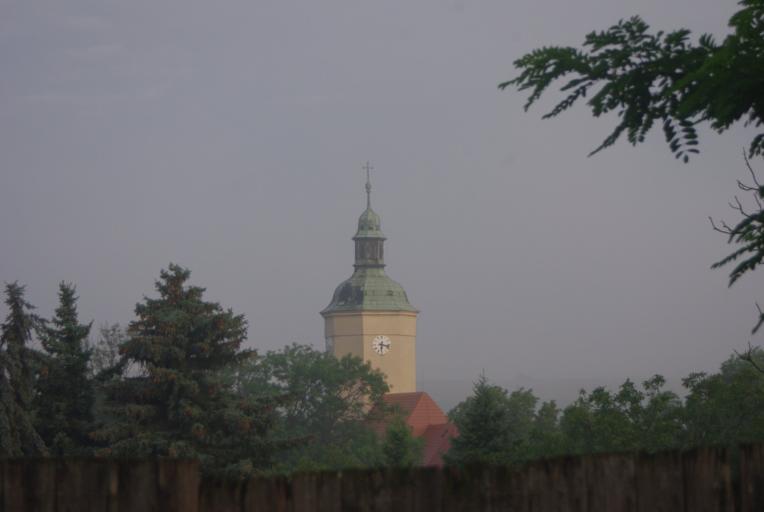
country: HU
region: Borsod-Abauj-Zemplen
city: Abaujszanto
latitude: 48.2754
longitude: 21.1884
